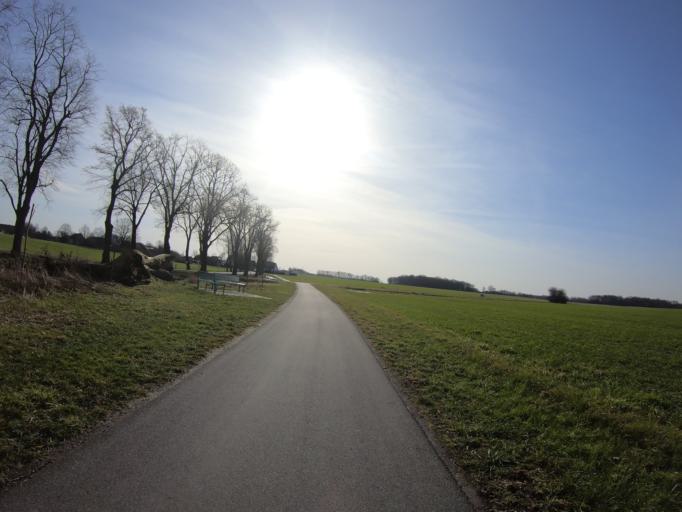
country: DE
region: Lower Saxony
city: Rotgesbuttel
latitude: 52.4062
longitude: 10.5624
